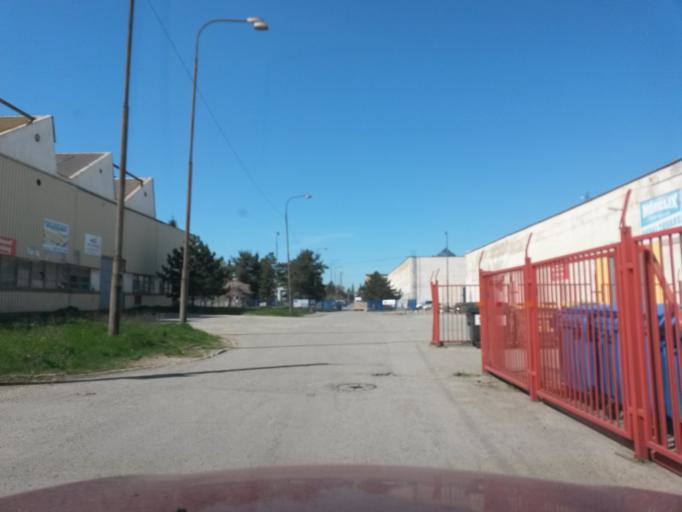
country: SK
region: Kosicky
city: Kosice
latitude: 48.6811
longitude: 21.2718
